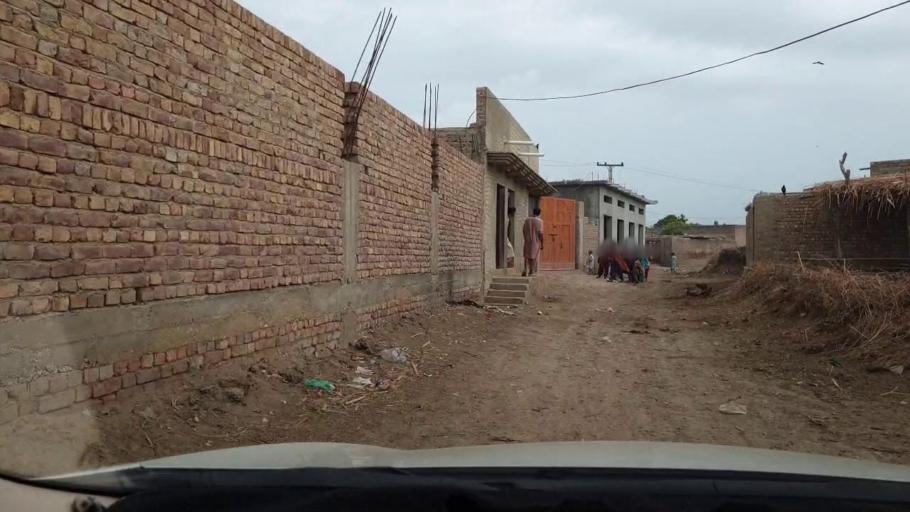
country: PK
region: Sindh
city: Tando Muhammad Khan
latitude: 25.1100
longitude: 68.6089
